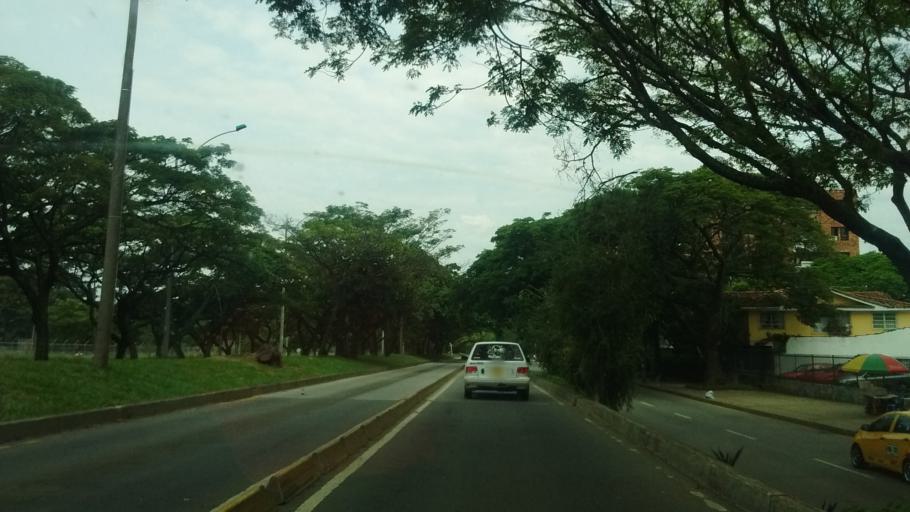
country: CO
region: Valle del Cauca
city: Cali
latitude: 3.3700
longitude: -76.5351
